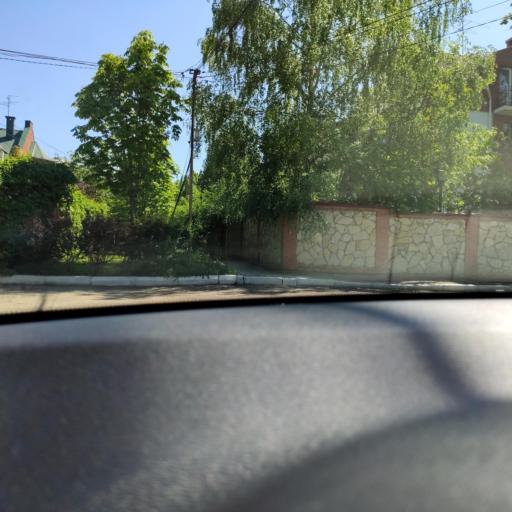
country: RU
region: Samara
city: Samara
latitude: 53.2402
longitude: 50.1748
